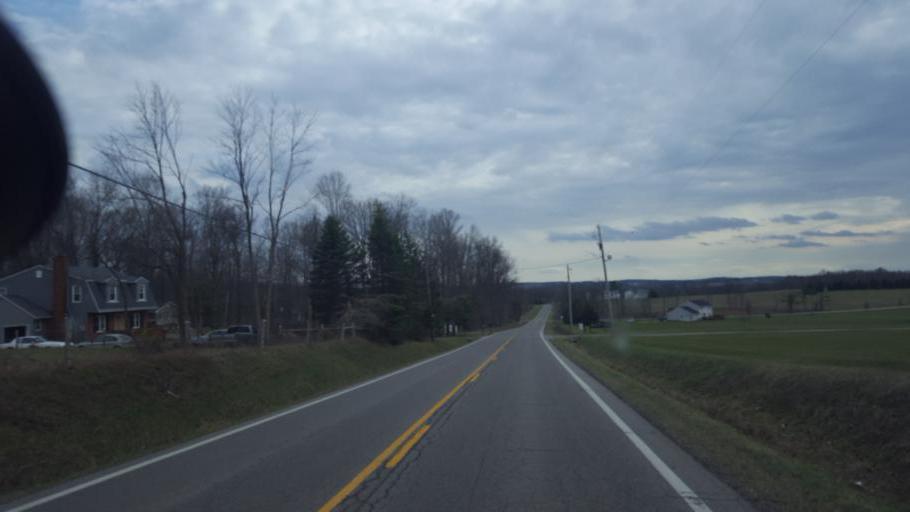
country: US
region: Ohio
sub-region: Richland County
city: Lexington
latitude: 40.6476
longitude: -82.5911
